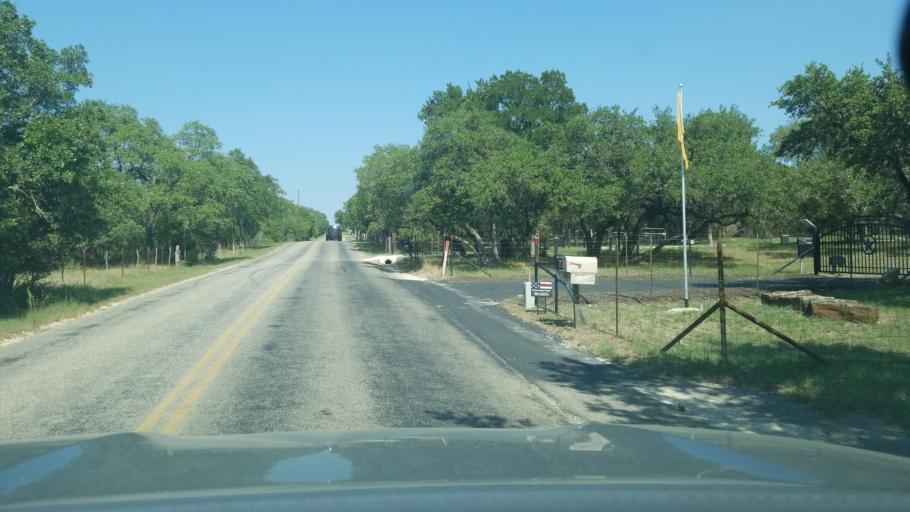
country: US
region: Texas
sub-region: Bexar County
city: Fair Oaks Ranch
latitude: 29.7856
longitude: -98.6443
